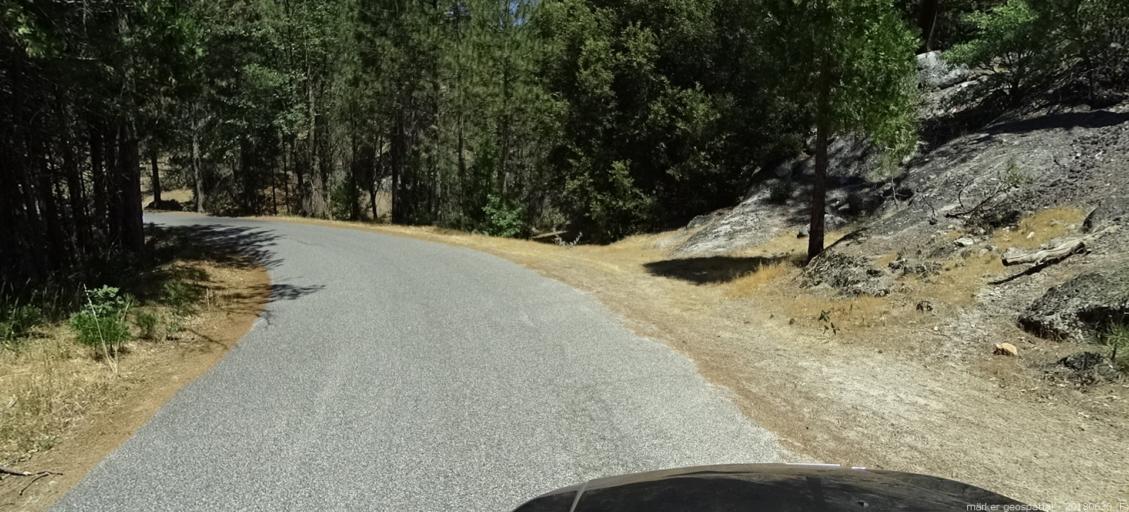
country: US
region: California
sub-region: Madera County
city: Oakhurst
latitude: 37.3746
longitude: -119.3552
